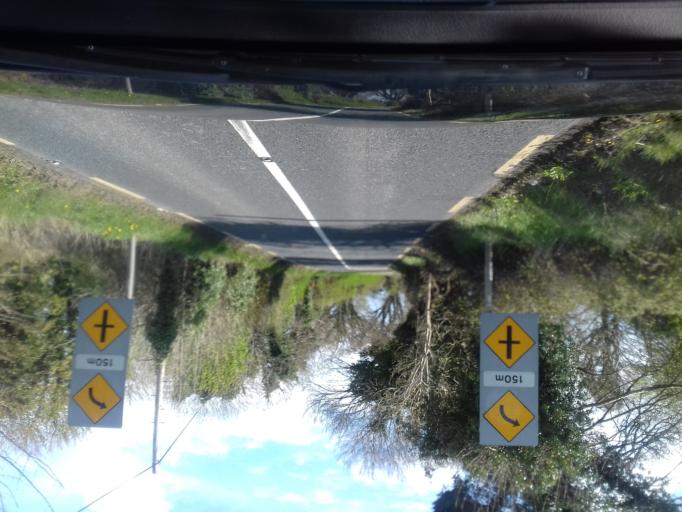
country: IE
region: Ulster
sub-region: County Donegal
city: Ballyshannon
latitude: 54.4805
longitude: -8.1069
